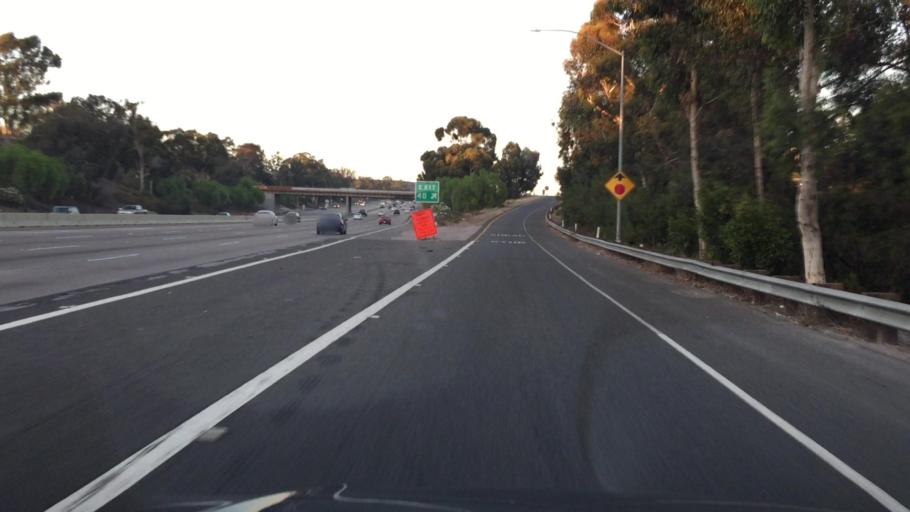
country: US
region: California
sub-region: San Diego County
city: National City
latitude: 32.7219
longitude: -117.0783
